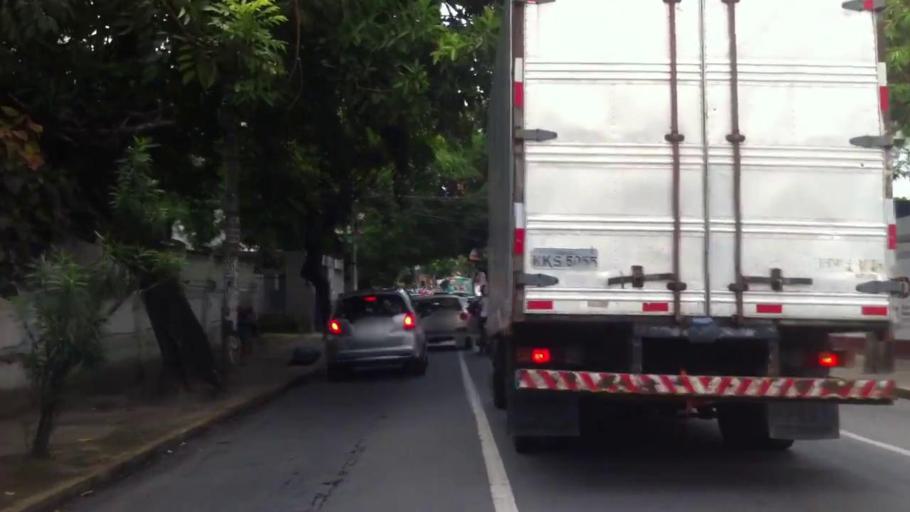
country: BR
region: Pernambuco
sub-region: Recife
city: Recife
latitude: -8.0471
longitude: -34.9007
